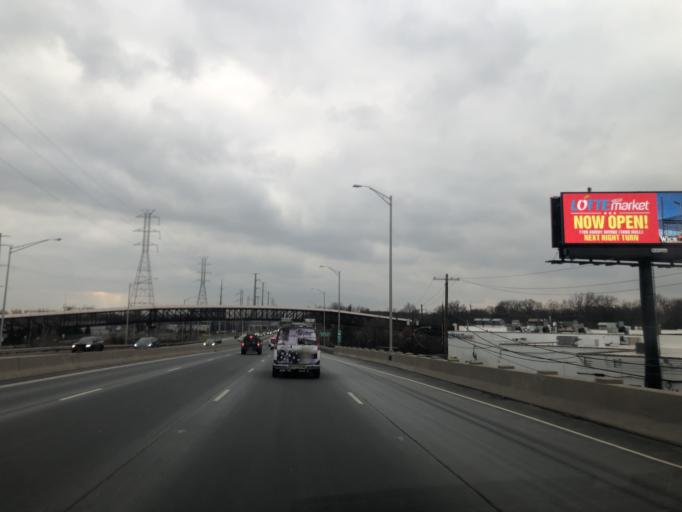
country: US
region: New Jersey
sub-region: Middlesex County
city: Metuchen
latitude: 40.5348
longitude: -74.3459
